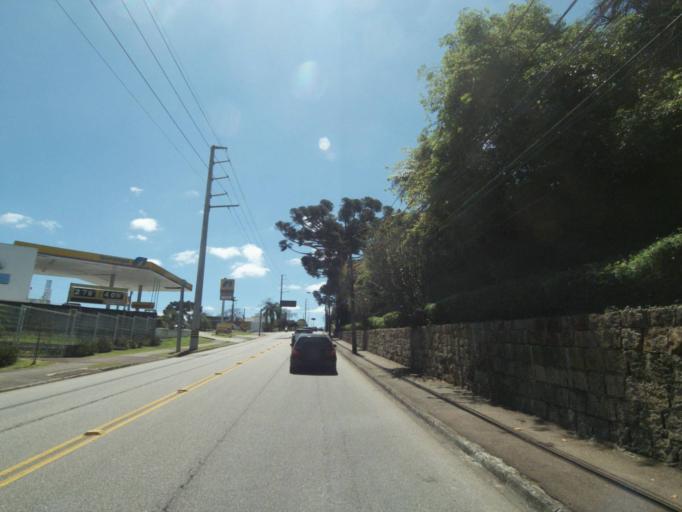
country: BR
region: Parana
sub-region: Curitiba
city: Curitiba
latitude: -25.3932
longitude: -49.2728
